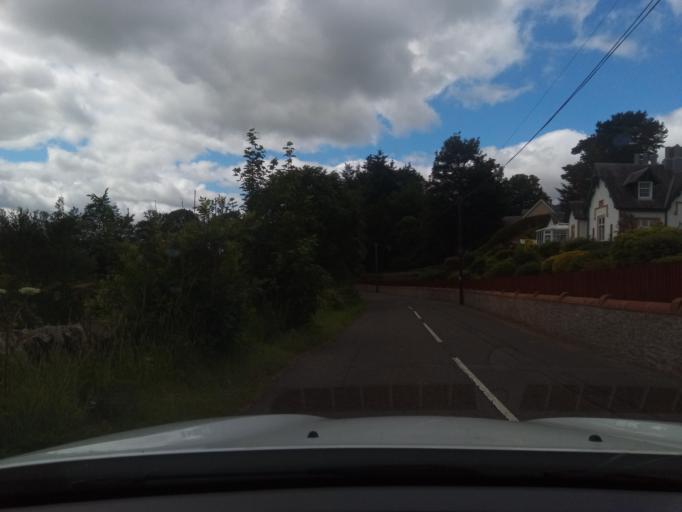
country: GB
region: Scotland
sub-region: The Scottish Borders
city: Selkirk
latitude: 55.5480
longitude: -2.8618
